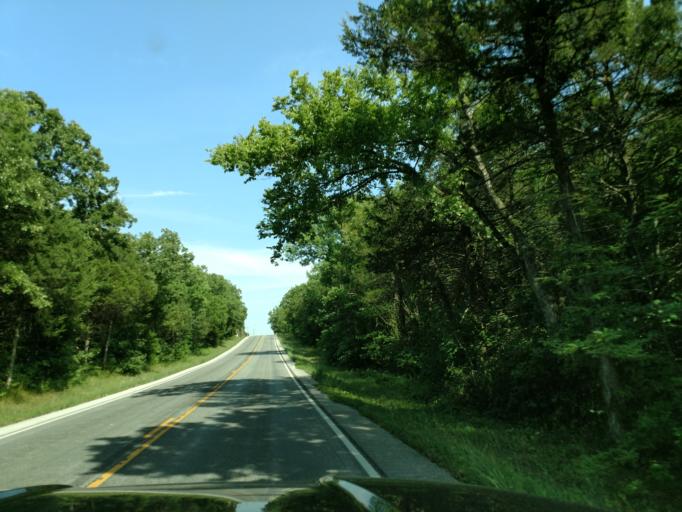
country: US
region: Missouri
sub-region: Barry County
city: Shell Knob
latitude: 36.6145
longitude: -93.5978
